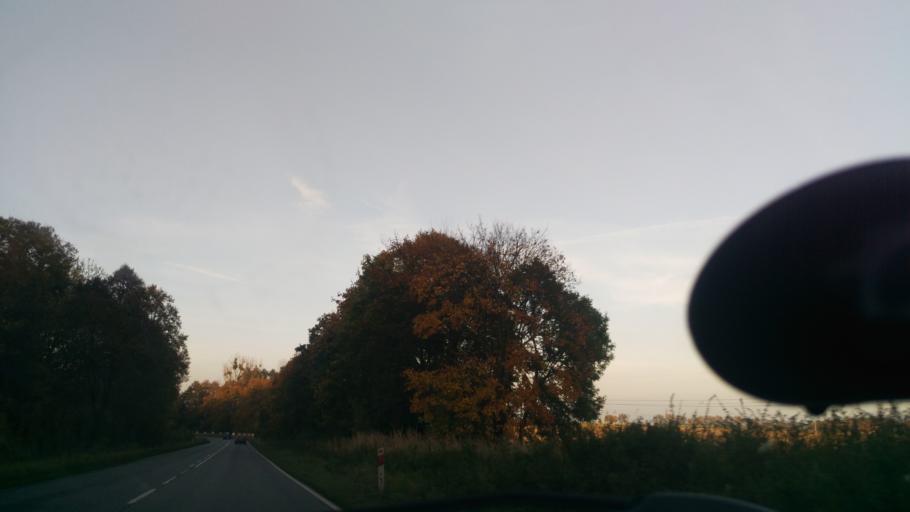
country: PL
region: West Pomeranian Voivodeship
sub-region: Powiat gryfinski
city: Stare Czarnowo
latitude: 53.3001
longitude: 14.7920
